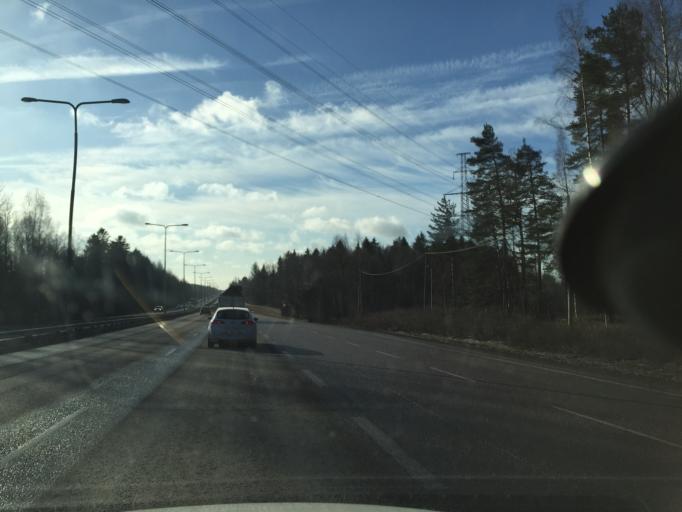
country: FI
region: Uusimaa
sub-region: Helsinki
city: Teekkarikylae
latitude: 60.2581
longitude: 24.8784
